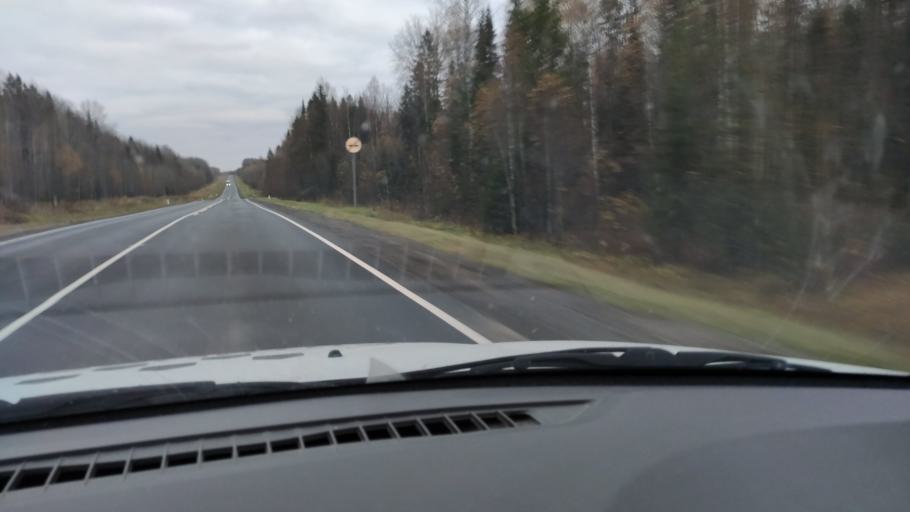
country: RU
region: Kirov
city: Lesnyye Polyany
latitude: 58.8011
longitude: 52.5491
